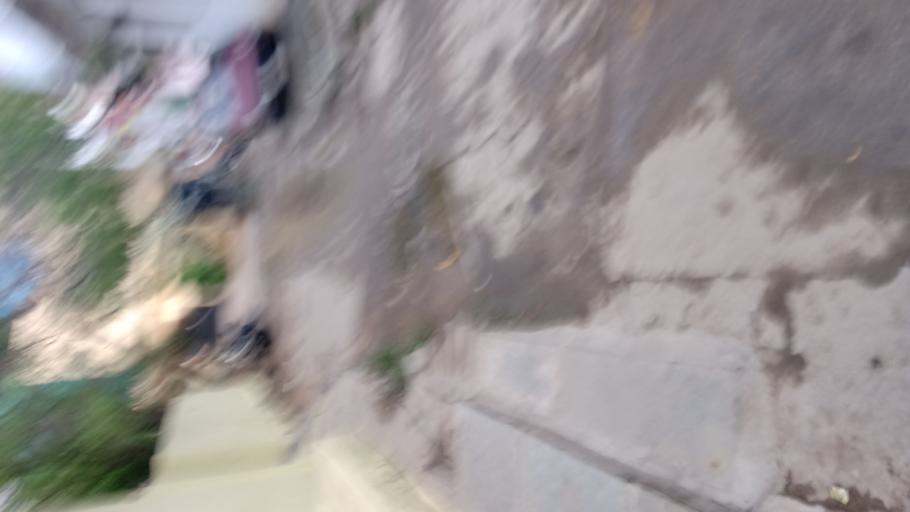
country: IN
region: Telangana
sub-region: Rangareddi
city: Uppal Kalan
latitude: 17.3967
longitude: 78.5379
